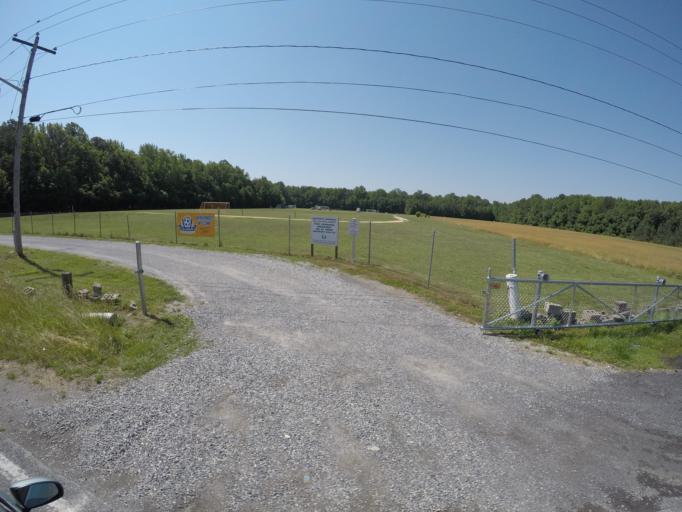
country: US
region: Delaware
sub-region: Sussex County
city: Georgetown
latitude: 38.6909
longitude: -75.3717
